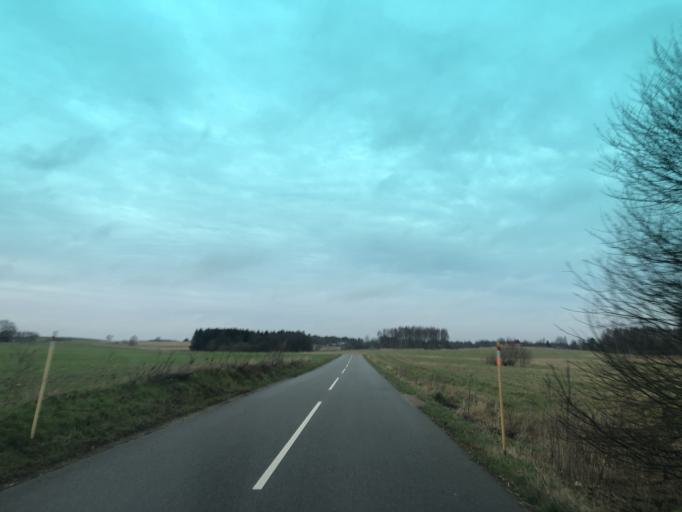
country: DK
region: Capital Region
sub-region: Frederikssund Kommune
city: Slangerup
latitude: 55.8605
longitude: 12.2293
